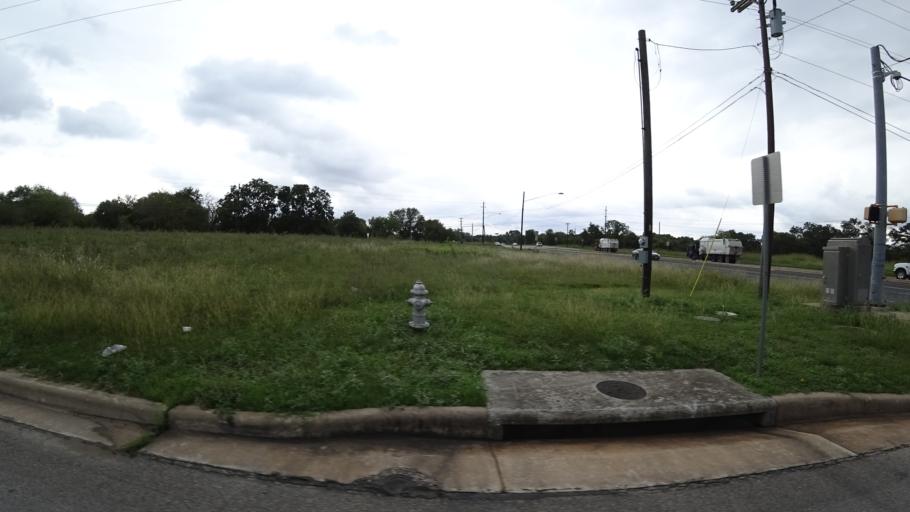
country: US
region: Texas
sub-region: Travis County
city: Onion Creek
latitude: 30.1689
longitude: -97.7386
